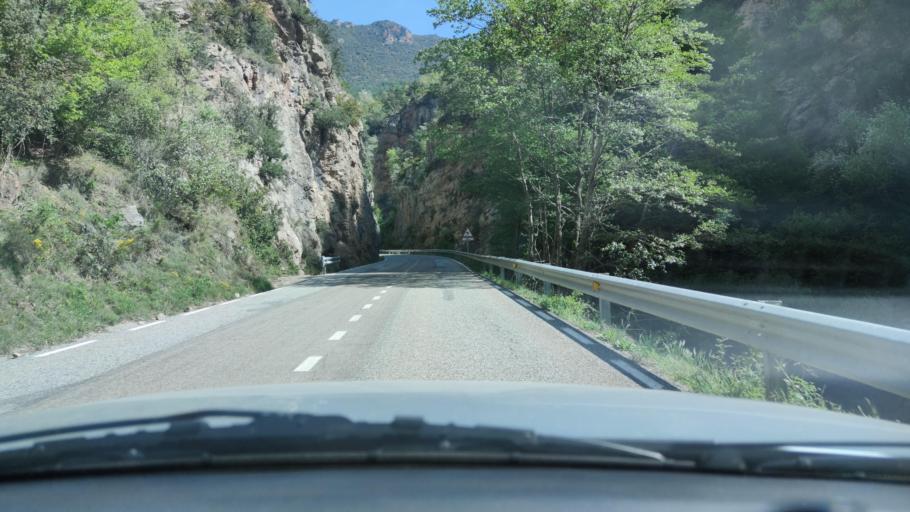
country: ES
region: Catalonia
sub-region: Provincia de Lleida
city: Coll de Nargo
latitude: 42.3084
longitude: 1.2890
